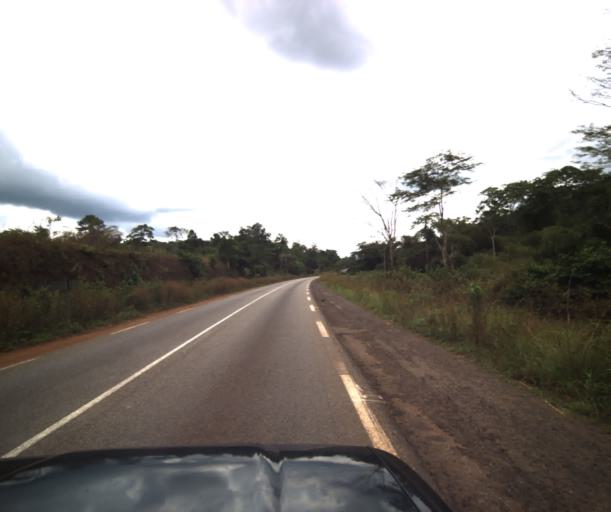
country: CM
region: Littoral
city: Edea
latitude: 3.8181
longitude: 10.3726
